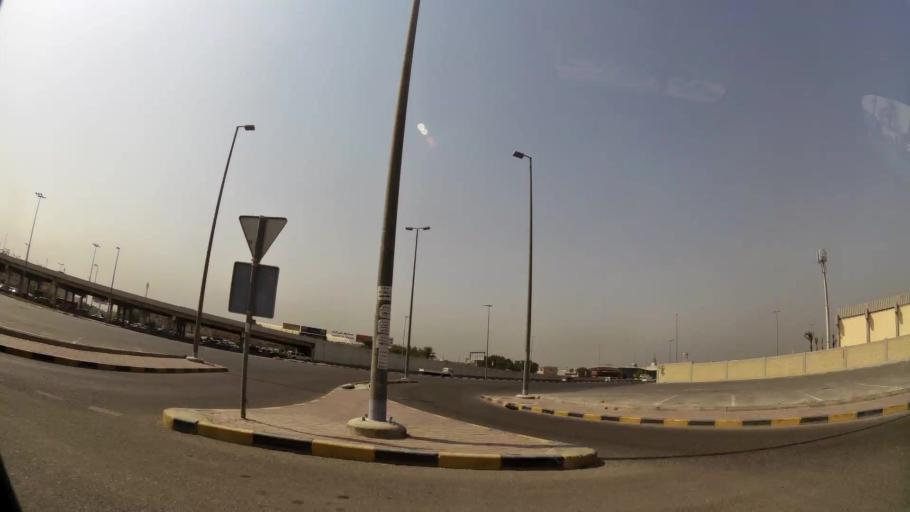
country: KW
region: Al Asimah
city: Ash Shamiyah
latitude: 29.3347
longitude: 47.9524
